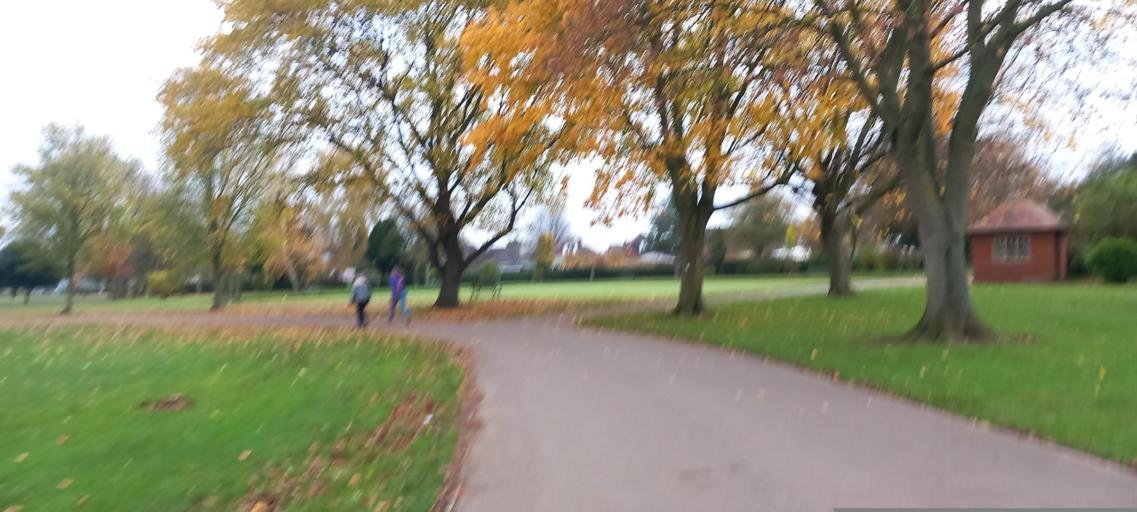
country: GB
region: England
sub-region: East Riding of Yorkshire
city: Airmyn
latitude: 53.7104
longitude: -0.8897
